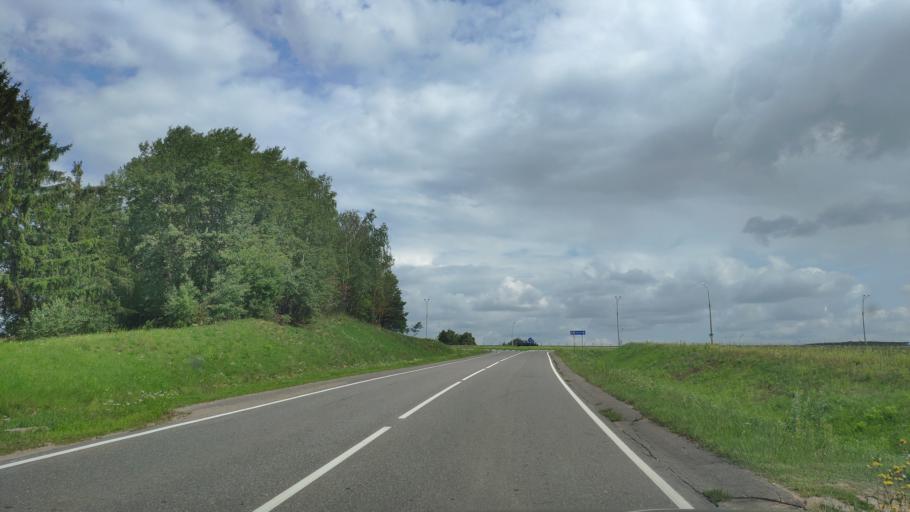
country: BY
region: Minsk
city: Zaslawye
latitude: 54.0074
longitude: 27.3068
